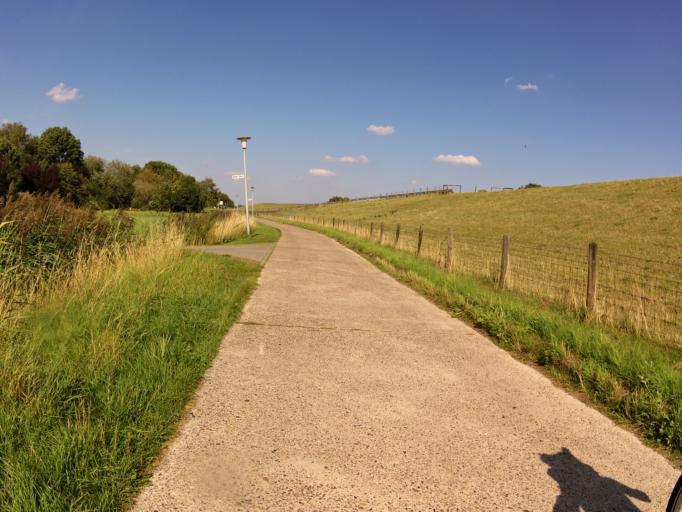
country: DE
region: Lower Saxony
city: Ovelgonne
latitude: 53.3945
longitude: 8.4599
